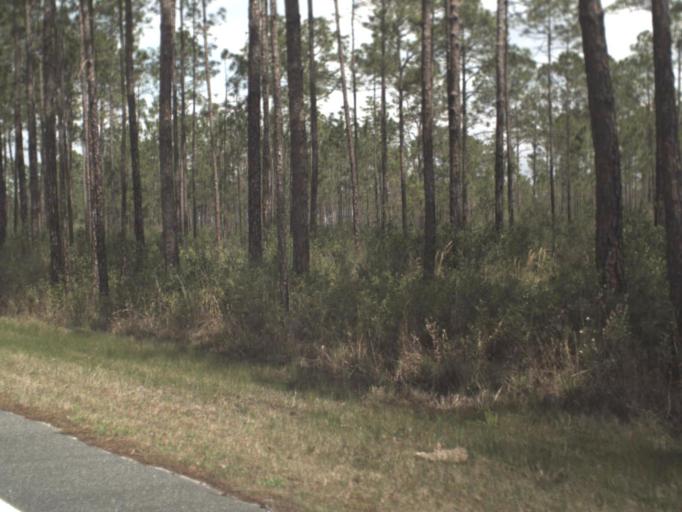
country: US
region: Florida
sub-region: Franklin County
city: Apalachicola
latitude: 29.9439
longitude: -84.9766
